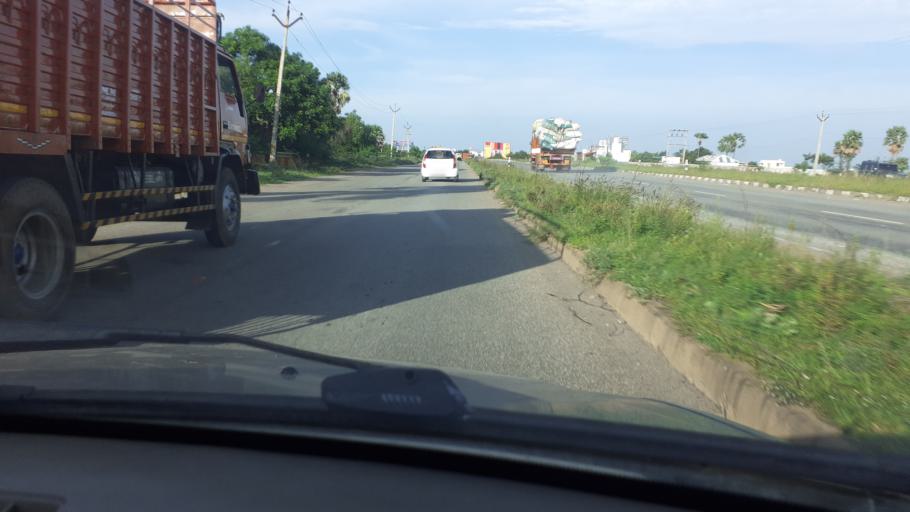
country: IN
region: Tamil Nadu
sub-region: Tirunelveli Kattabo
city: Tirunelveli
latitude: 8.6518
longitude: 77.7116
